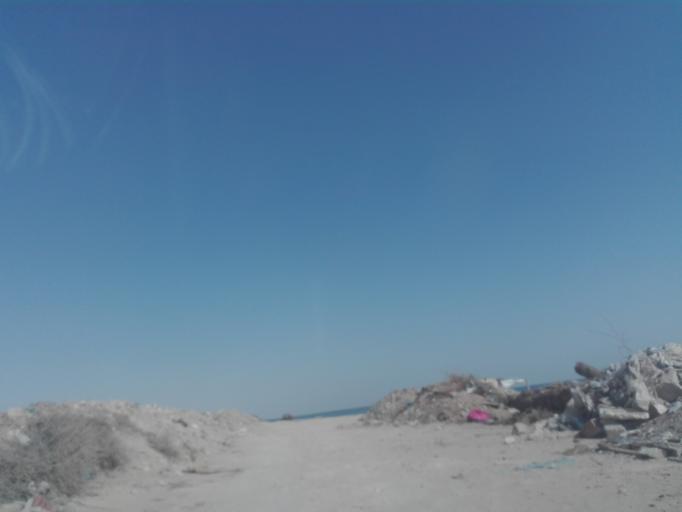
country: TN
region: Qabis
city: Gabes
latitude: 33.9630
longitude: 10.0657
